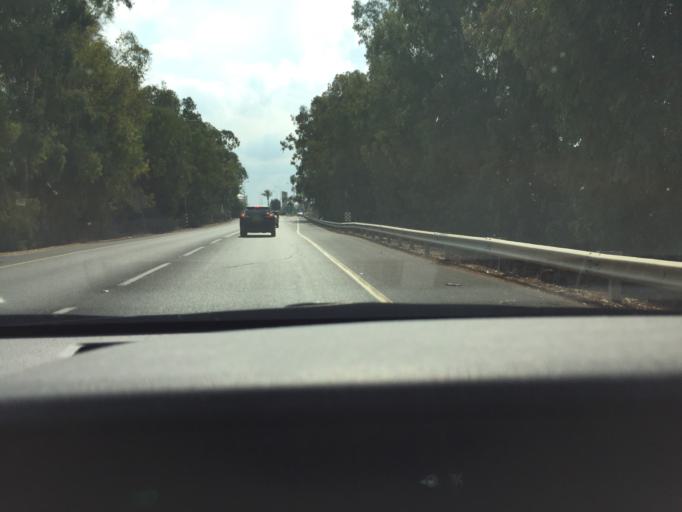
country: IL
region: Central District
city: Yehud
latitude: 31.9937
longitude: 34.9048
